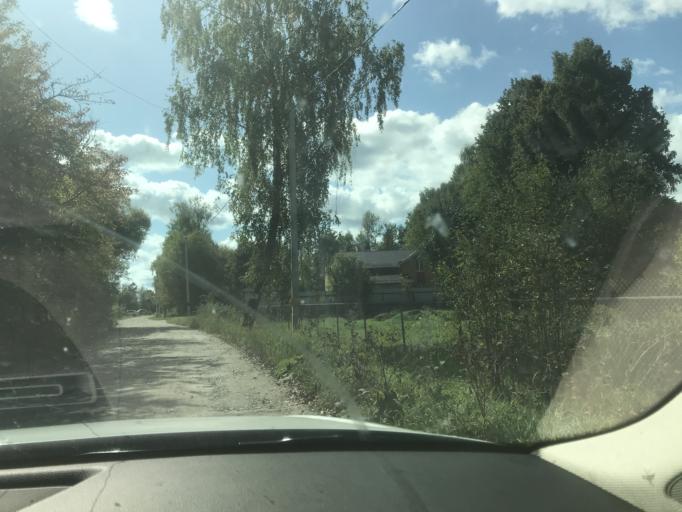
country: RU
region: Kaluga
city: Kondrovo
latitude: 54.7829
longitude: 35.9468
